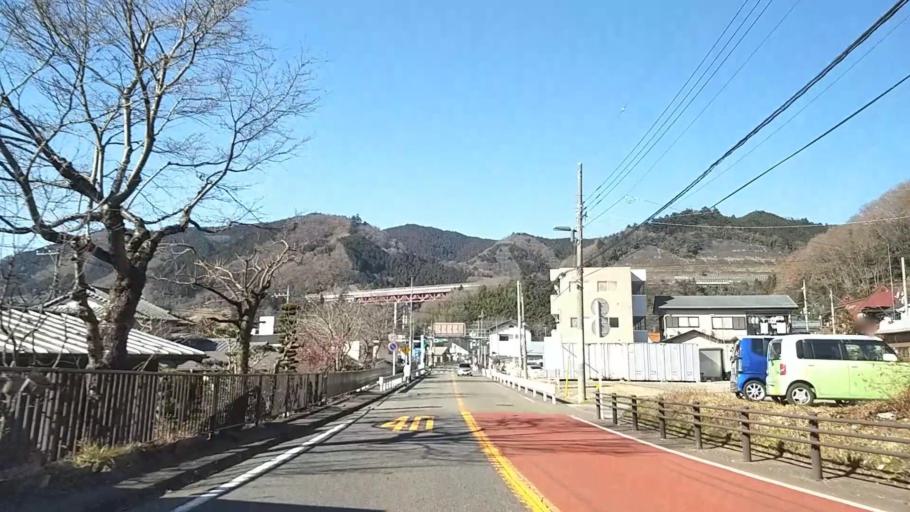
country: JP
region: Yamanashi
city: Uenohara
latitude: 35.6205
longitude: 139.2063
